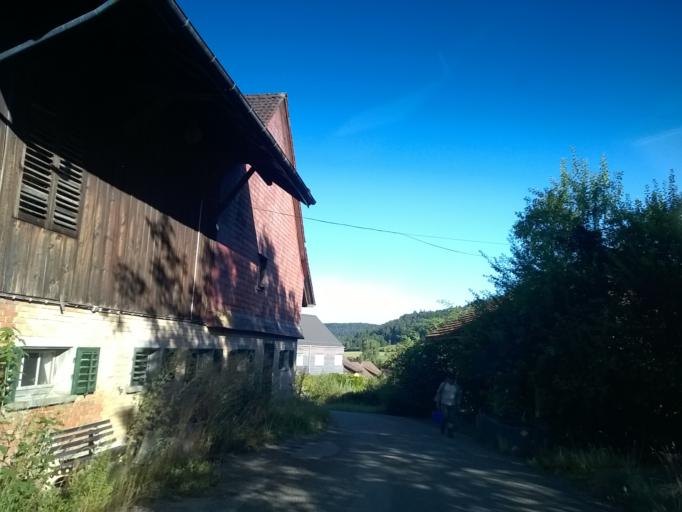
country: CH
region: Zurich
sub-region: Bezirk Buelach
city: Embrach / Embrach (Dorfkern)
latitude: 47.4917
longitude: 8.5933
